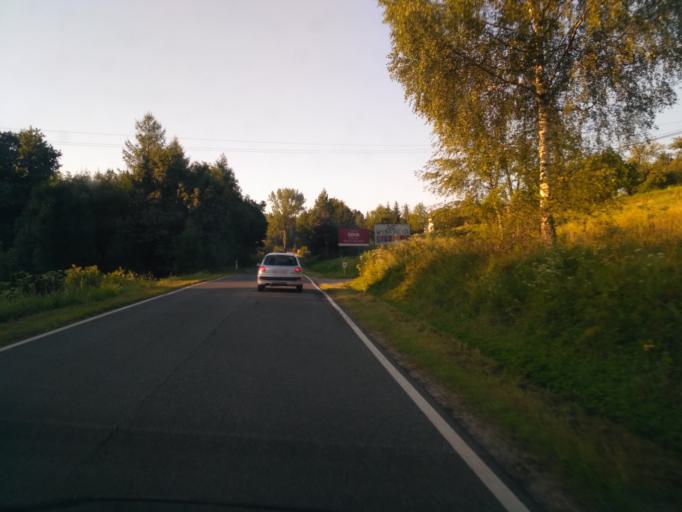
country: PL
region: Subcarpathian Voivodeship
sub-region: Powiat krosnienski
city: Korczyna
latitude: 49.7485
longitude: 21.8029
